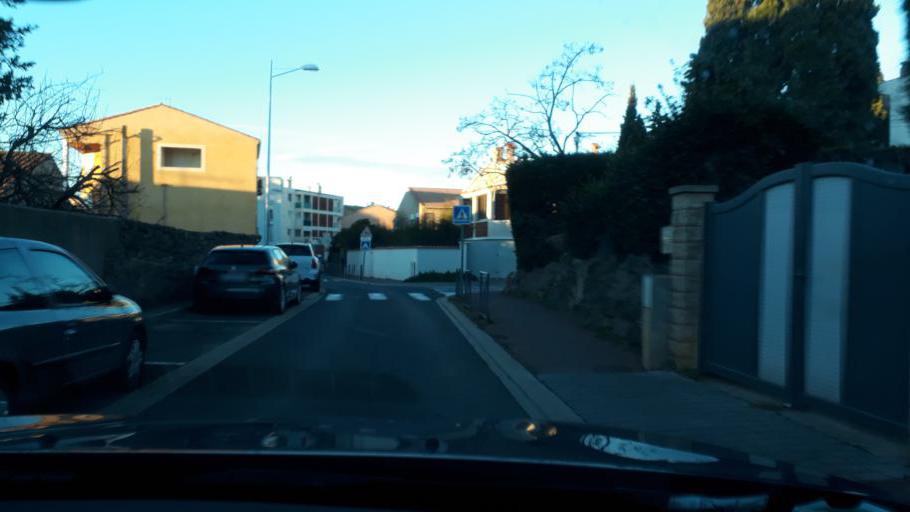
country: FR
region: Languedoc-Roussillon
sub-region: Departement de l'Herault
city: Agde
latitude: 43.3081
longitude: 3.4695
